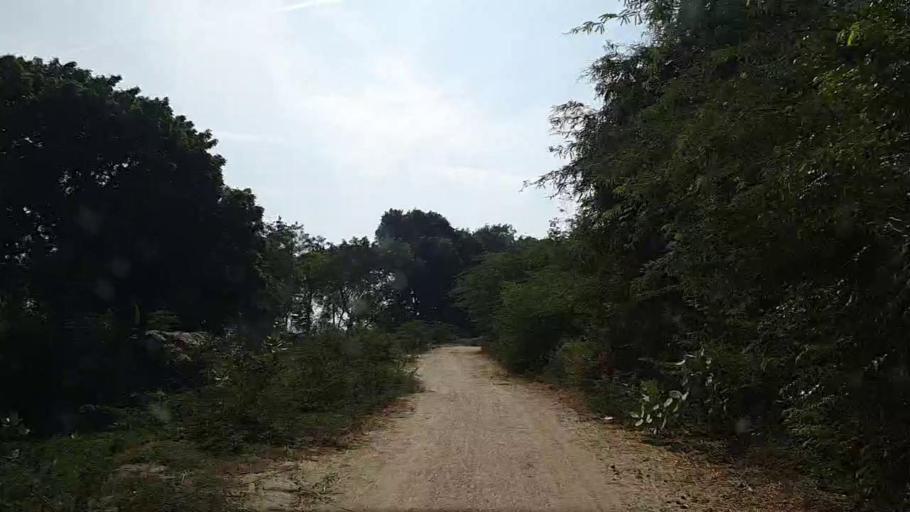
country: PK
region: Sindh
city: Daro Mehar
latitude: 24.7079
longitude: 68.1598
